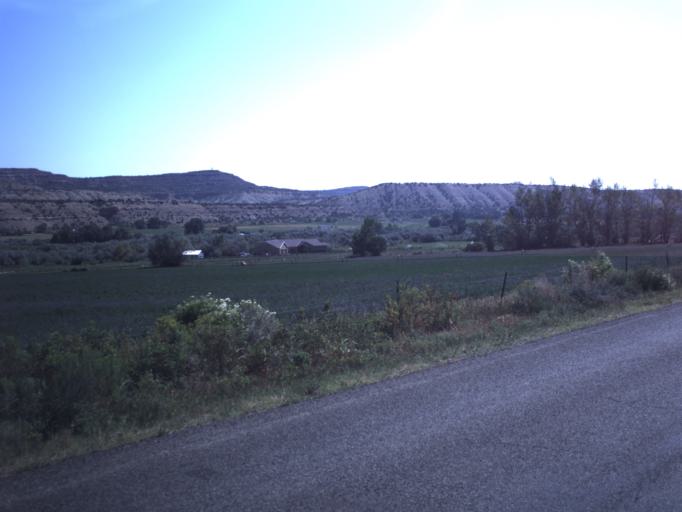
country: US
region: Utah
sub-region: Duchesne County
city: Duchesne
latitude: 40.2722
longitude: -110.4534
